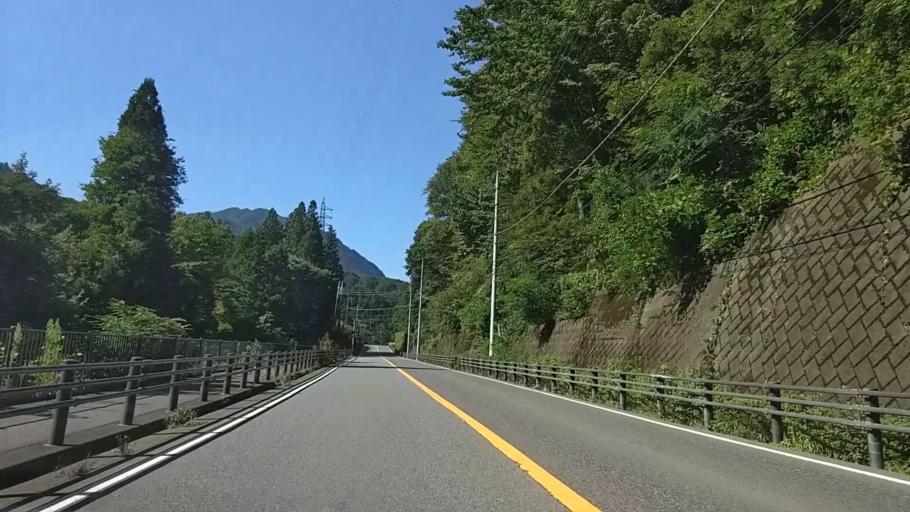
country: JP
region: Gunma
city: Annaka
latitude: 36.3326
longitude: 138.7144
